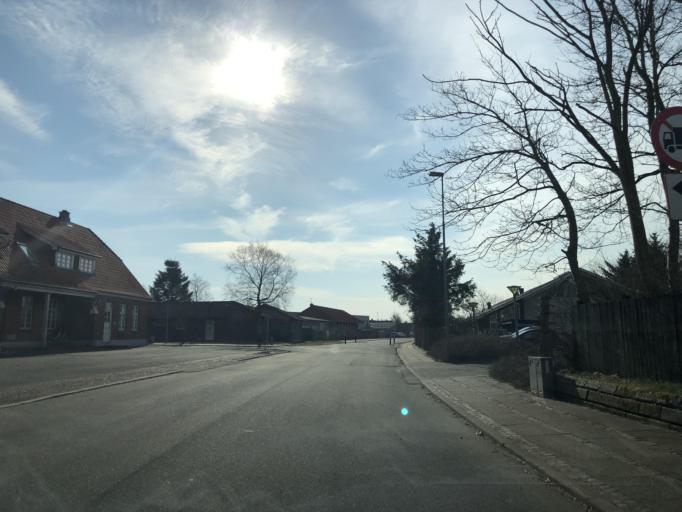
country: DK
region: Central Jutland
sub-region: Holstebro Kommune
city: Holstebro
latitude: 56.3522
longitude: 8.6136
